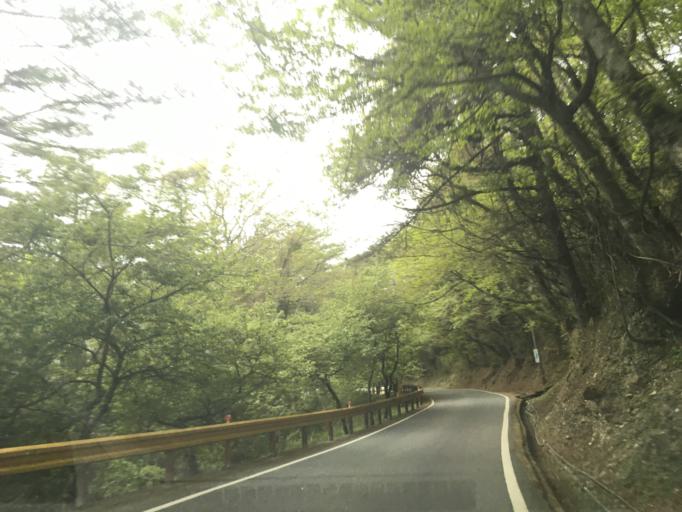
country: TW
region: Taiwan
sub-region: Hualien
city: Hualian
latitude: 24.1859
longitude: 121.3411
